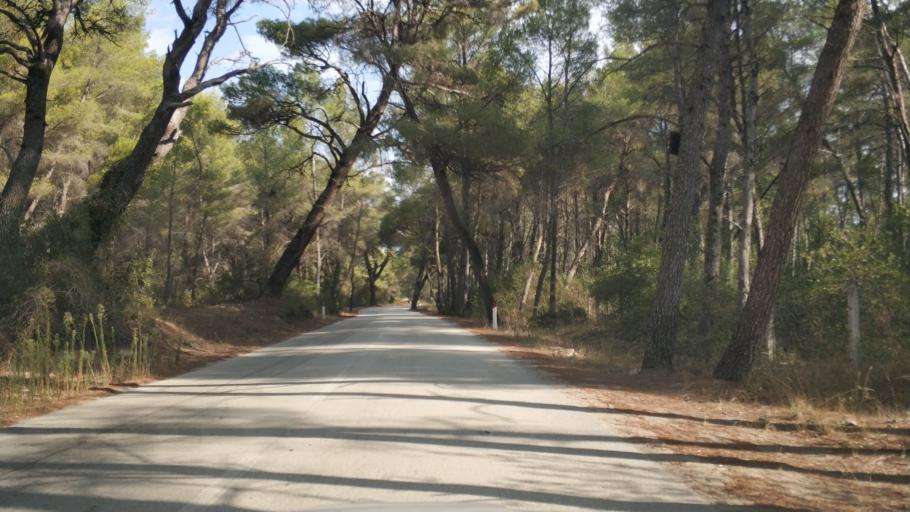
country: AL
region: Fier
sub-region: Rrethi i Lushnjes
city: Divjake
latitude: 40.9780
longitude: 19.4815
